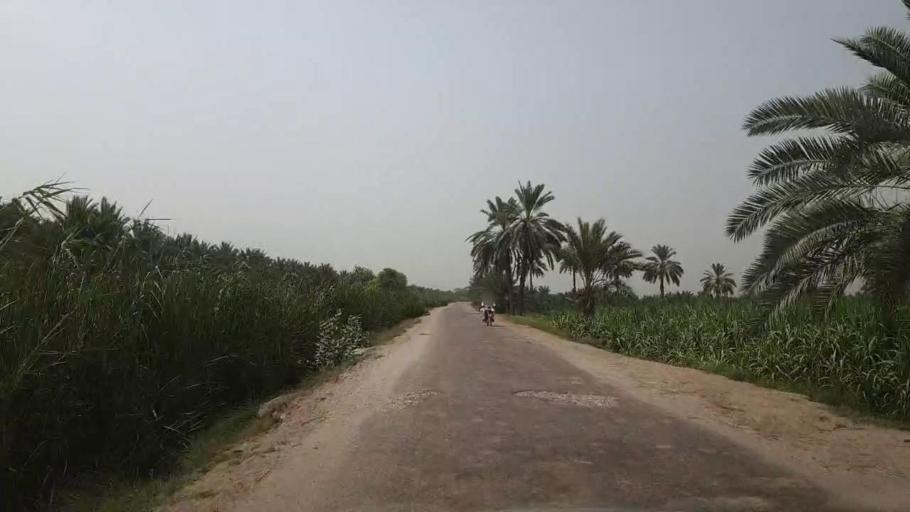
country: PK
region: Sindh
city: Gambat
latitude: 27.3996
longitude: 68.5517
